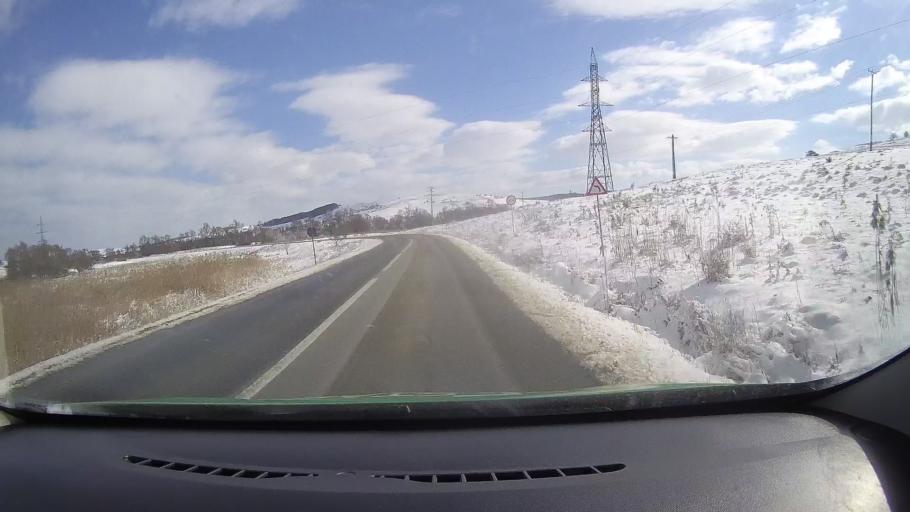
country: RO
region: Sibiu
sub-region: Comuna Barghis
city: Barghis
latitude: 45.9618
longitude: 24.5629
